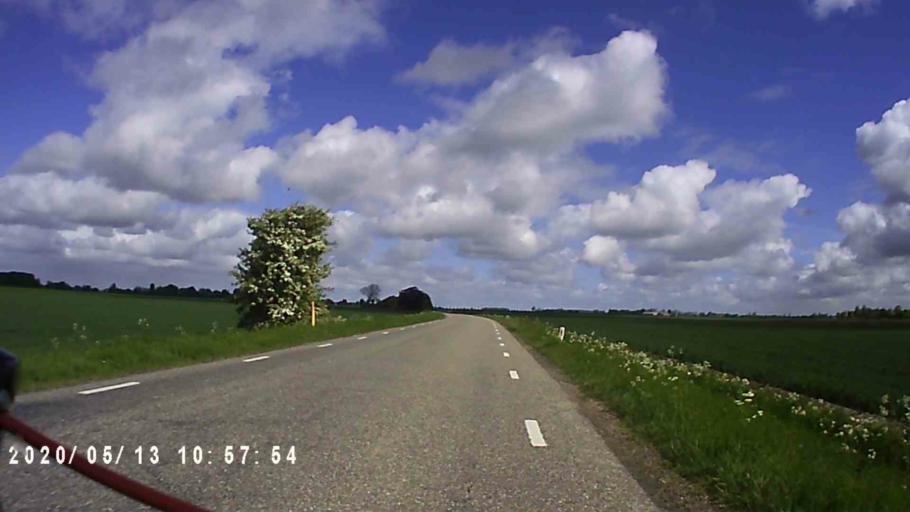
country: NL
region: Groningen
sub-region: Gemeente Zuidhorn
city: Grijpskerk
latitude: 53.2748
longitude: 6.3336
